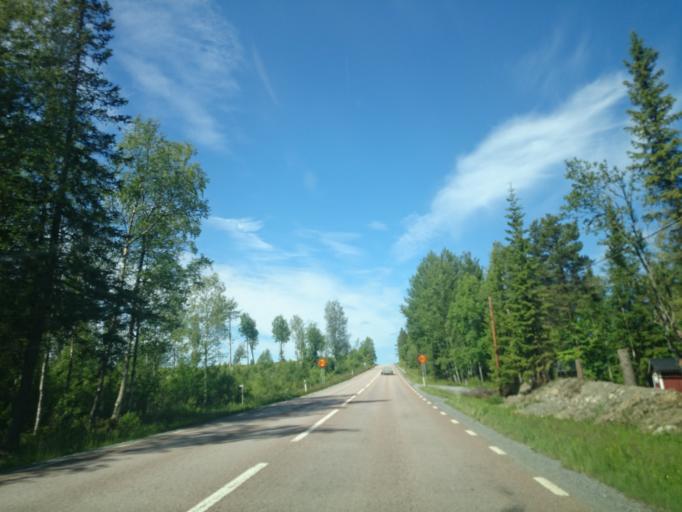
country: SE
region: Jaemtland
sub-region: OEstersunds Kommun
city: Brunflo
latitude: 63.0187
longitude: 14.9354
